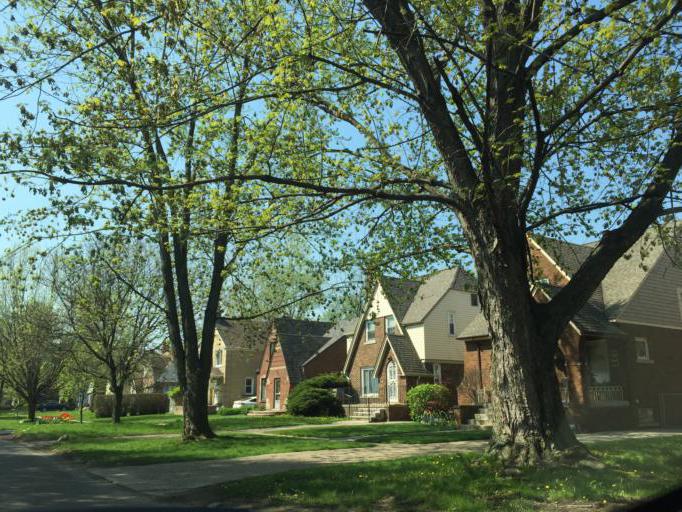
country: US
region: Michigan
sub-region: Oakland County
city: Southfield
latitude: 42.4132
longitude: -83.2278
